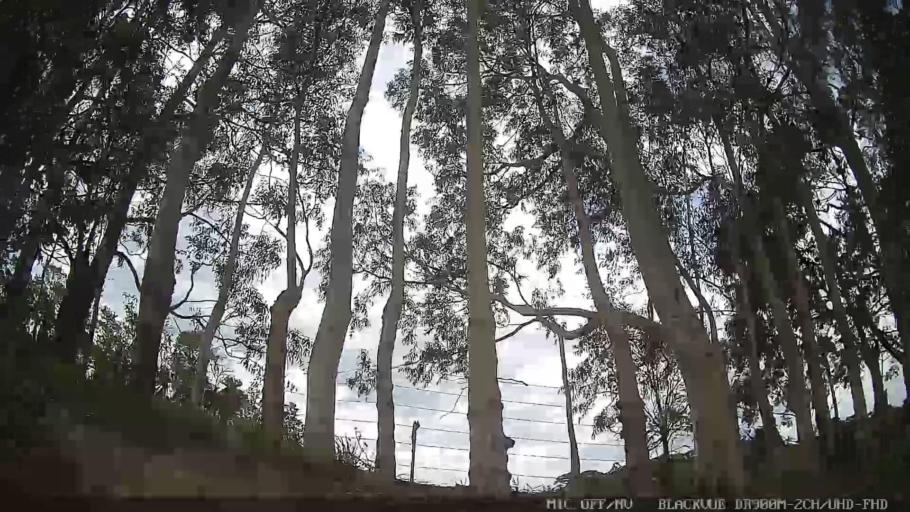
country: BR
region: Sao Paulo
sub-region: Serra Negra
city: Serra Negra
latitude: -22.6148
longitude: -46.7465
